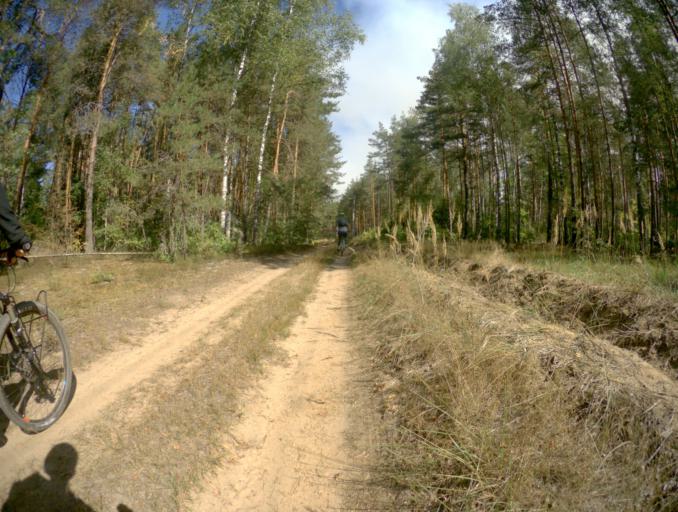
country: RU
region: Vladimir
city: Petushki
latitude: 55.8674
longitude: 39.3859
